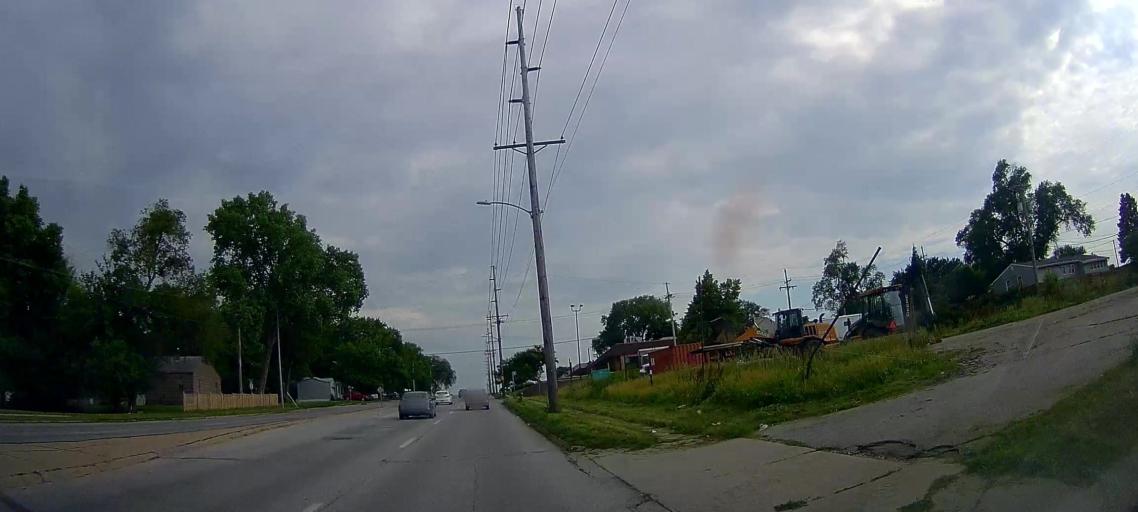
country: US
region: Nebraska
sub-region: Douglas County
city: Ralston
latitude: 41.2819
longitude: -96.0240
